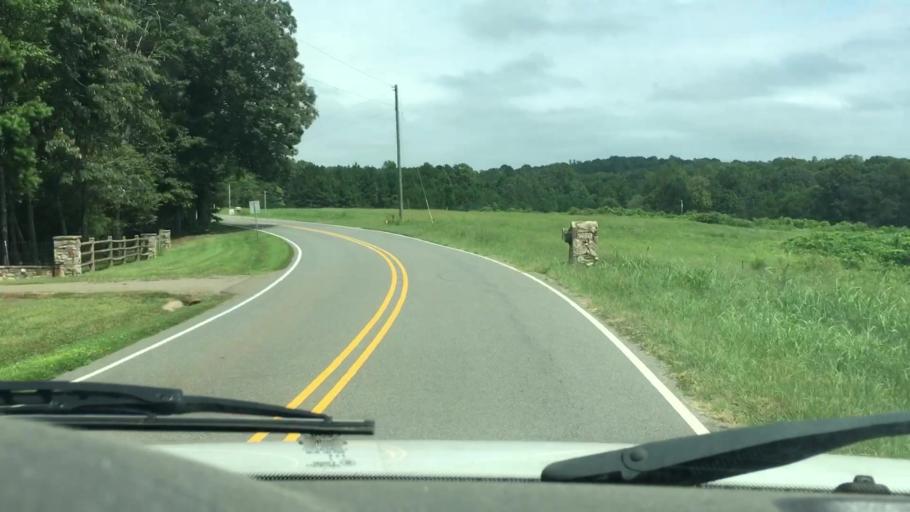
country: US
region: North Carolina
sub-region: Gaston County
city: Davidson
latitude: 35.5009
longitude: -80.8143
